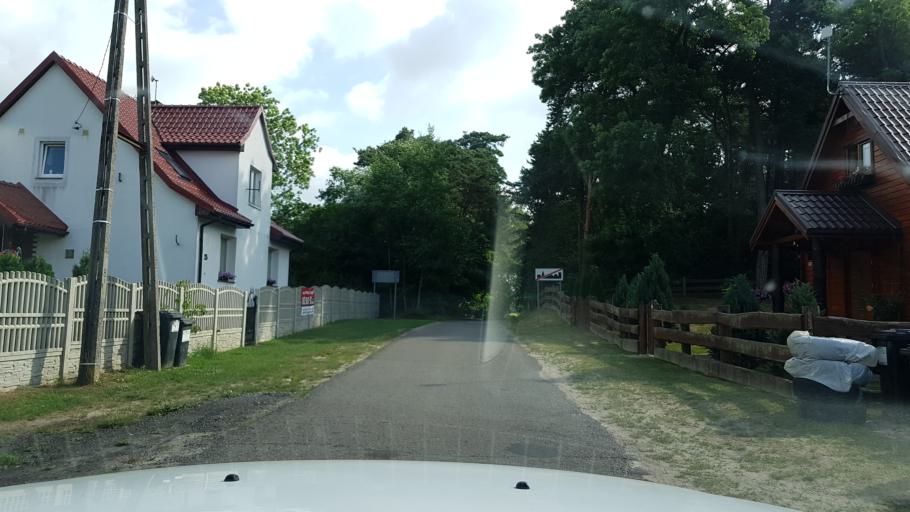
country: PL
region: West Pomeranian Voivodeship
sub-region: Powiat gryfinski
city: Gryfino
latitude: 53.2083
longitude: 14.5822
